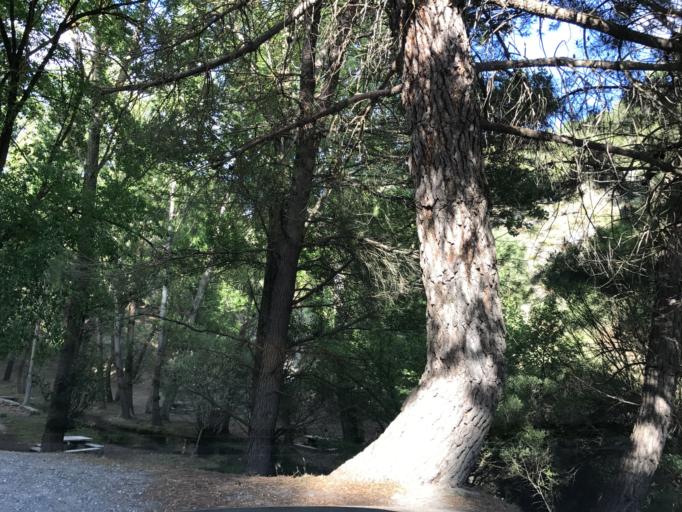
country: ES
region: Andalusia
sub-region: Provincia de Granada
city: Quentar
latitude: 37.2303
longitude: -3.4085
